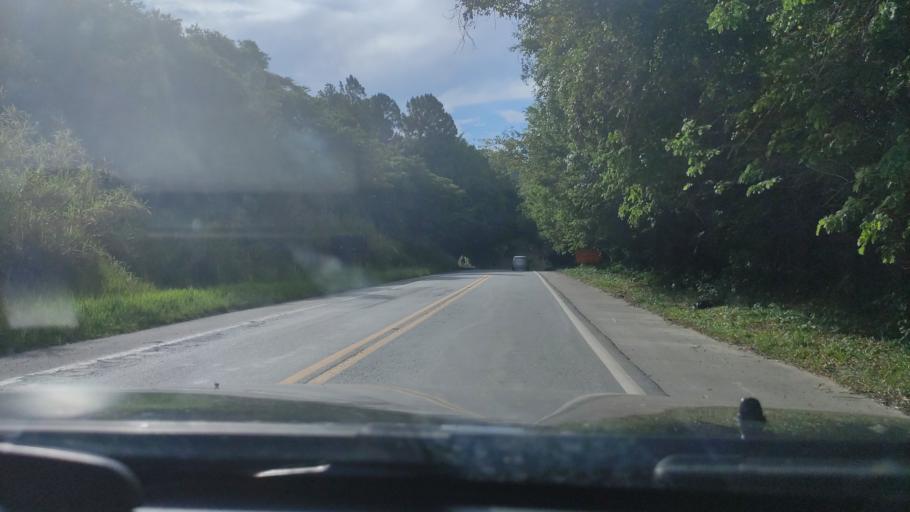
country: BR
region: Sao Paulo
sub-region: Aguas De Lindoia
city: Aguas de Lindoia
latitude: -22.5185
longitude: -46.6658
